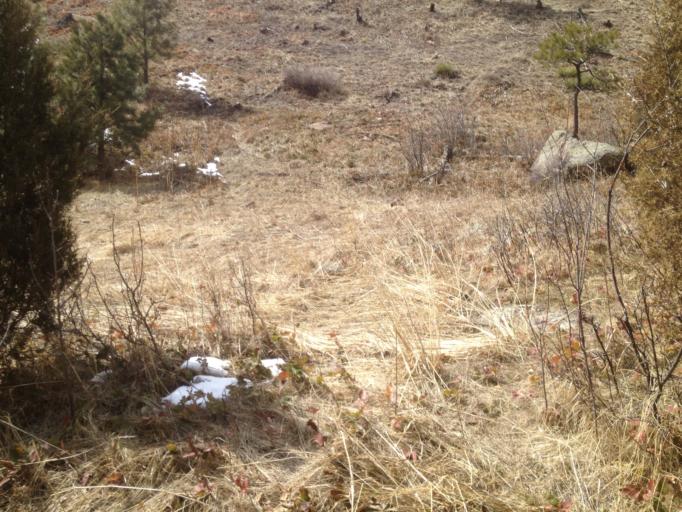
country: US
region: Colorado
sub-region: Boulder County
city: Boulder
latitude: 39.9331
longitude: -105.2953
